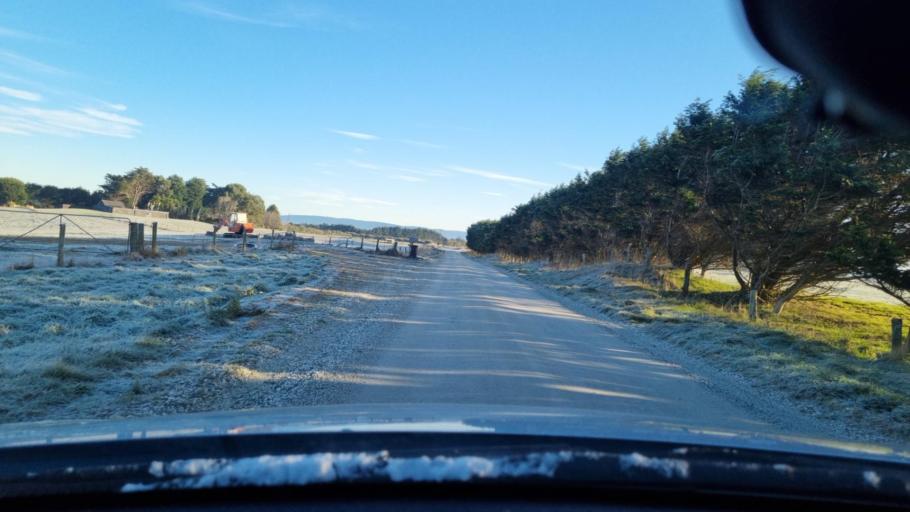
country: NZ
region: Southland
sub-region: Invercargill City
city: Invercargill
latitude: -46.4185
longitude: 168.2647
